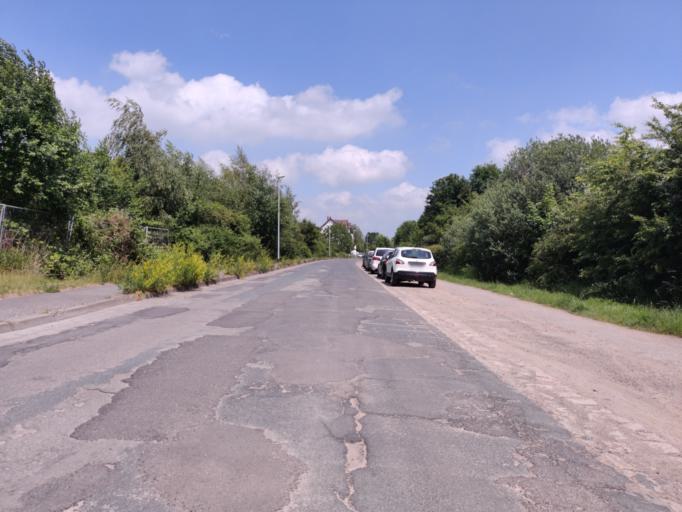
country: DE
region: Lower Saxony
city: Hildesheim
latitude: 52.1724
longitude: 9.9600
